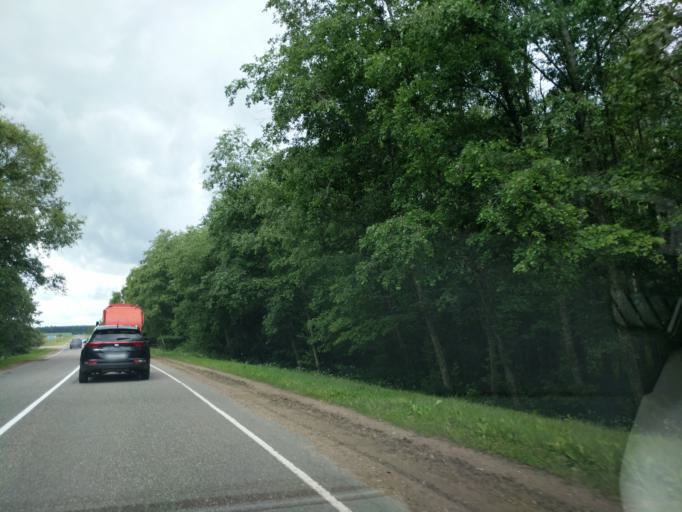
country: BY
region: Minsk
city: Il'ya
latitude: 54.4727
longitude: 27.2719
